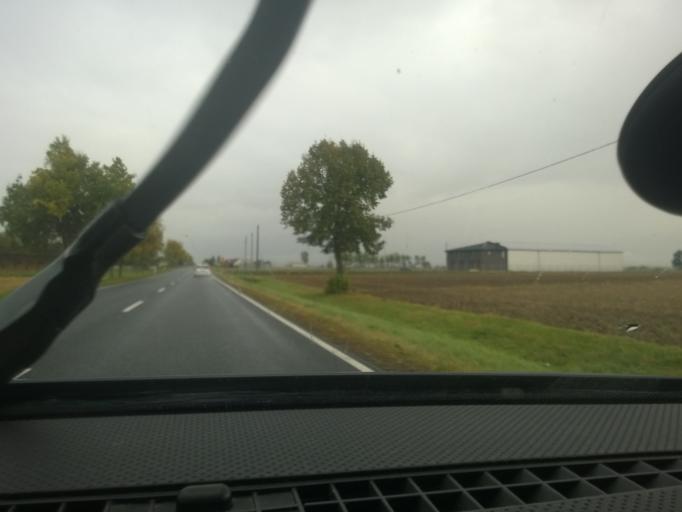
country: PL
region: Lodz Voivodeship
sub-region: Powiat sieradzki
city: Blaszki
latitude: 51.6763
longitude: 18.3559
